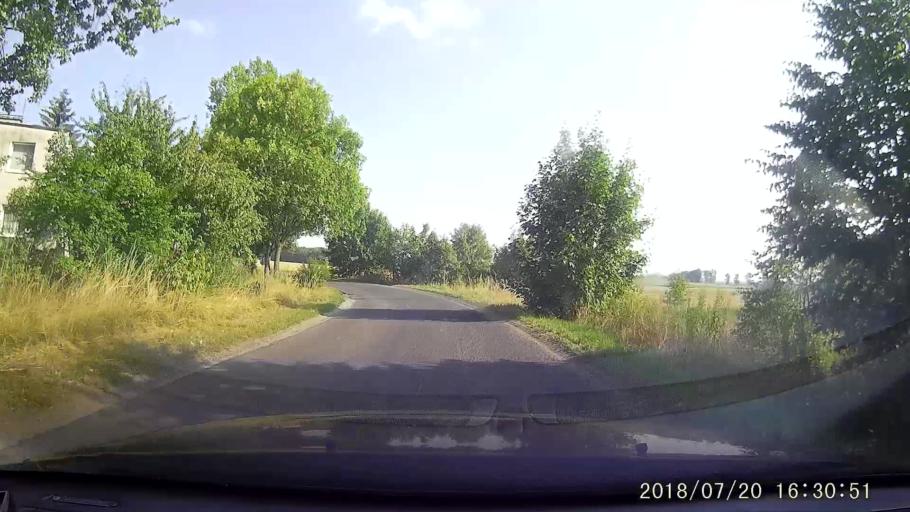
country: PL
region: Lower Silesian Voivodeship
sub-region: Powiat zgorzelecki
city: Sulikow
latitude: 51.1020
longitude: 15.0693
